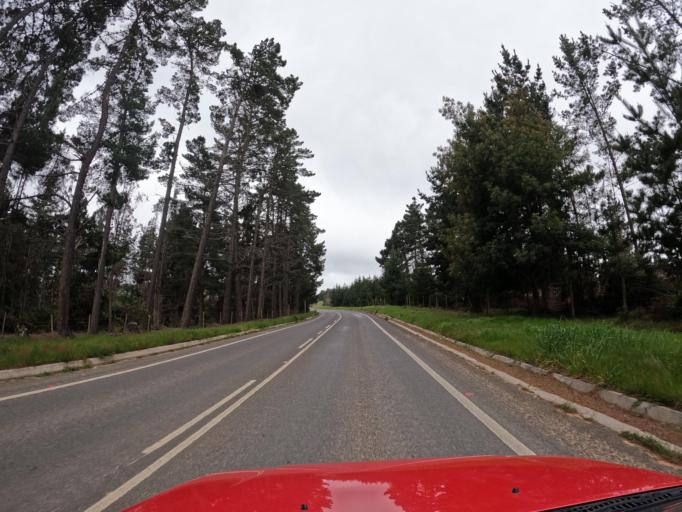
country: CL
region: O'Higgins
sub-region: Provincia de Colchagua
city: Santa Cruz
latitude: -34.5568
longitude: -72.0184
